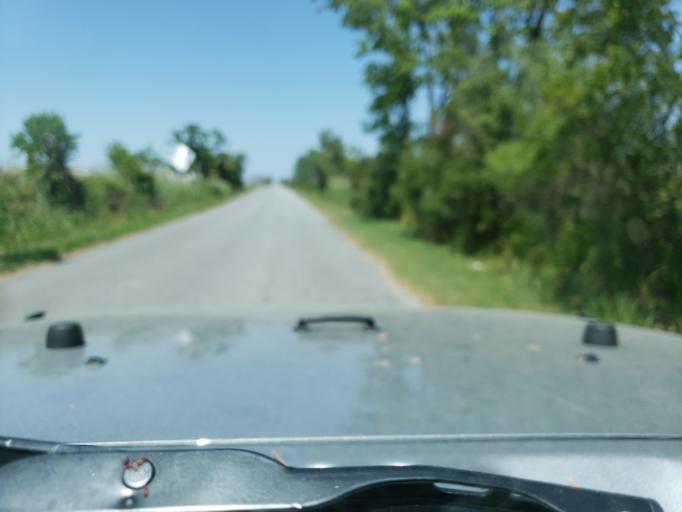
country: US
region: Georgia
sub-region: Chatham County
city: Thunderbolt
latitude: 32.0709
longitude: -81.0481
